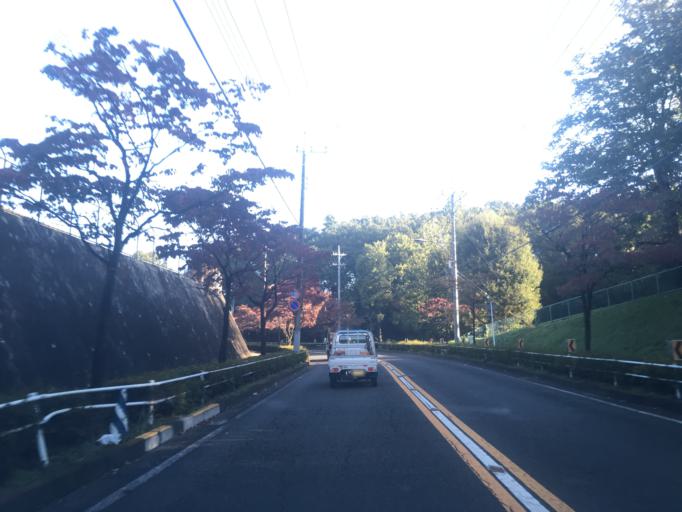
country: JP
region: Tokyo
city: Hino
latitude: 35.6824
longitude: 139.3583
